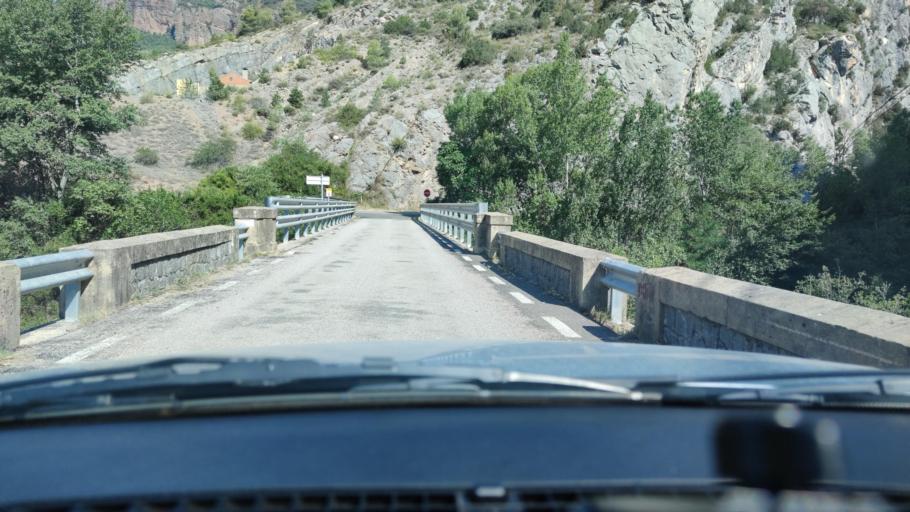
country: ES
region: Catalonia
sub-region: Provincia de Lleida
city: Senterada
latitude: 42.2865
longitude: 0.9371
